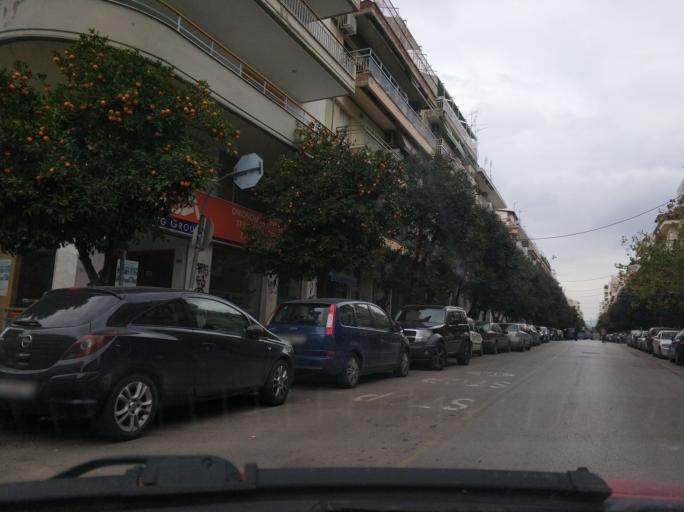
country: GR
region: Central Macedonia
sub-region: Nomos Thessalonikis
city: Triandria
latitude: 40.5997
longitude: 22.9633
